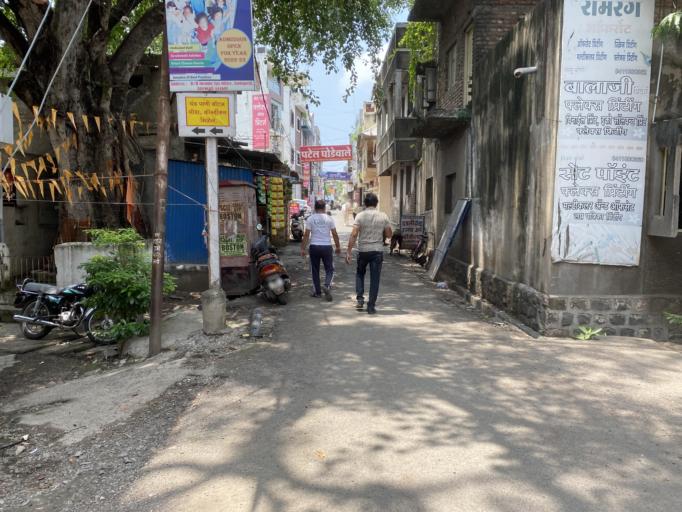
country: IN
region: Maharashtra
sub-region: Amravati Division
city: Amravati
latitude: 20.9273
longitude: 77.7514
